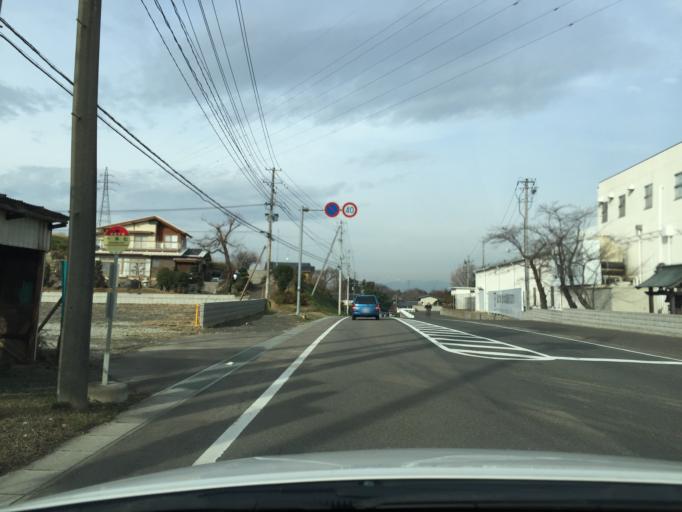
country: JP
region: Fukushima
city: Fukushima-shi
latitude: 37.6974
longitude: 140.4615
